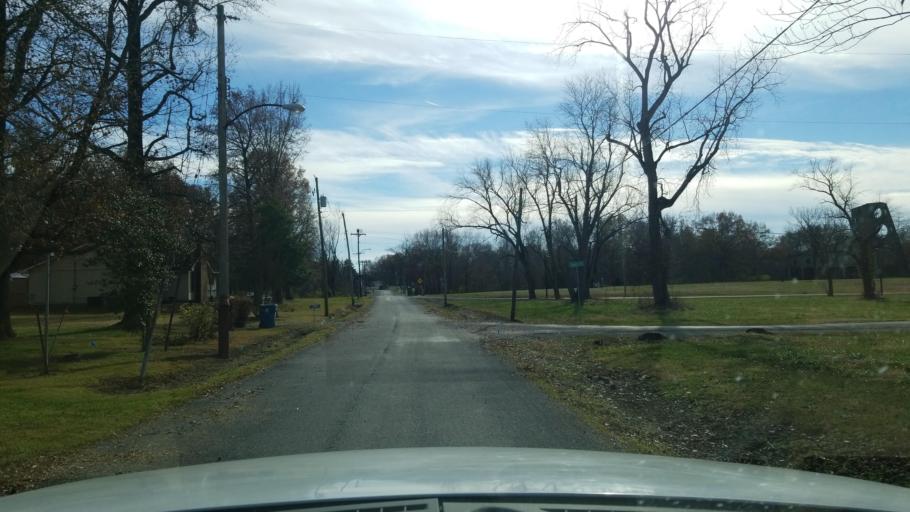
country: US
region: Illinois
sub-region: Saline County
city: Harrisburg
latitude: 37.7673
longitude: -88.5171
